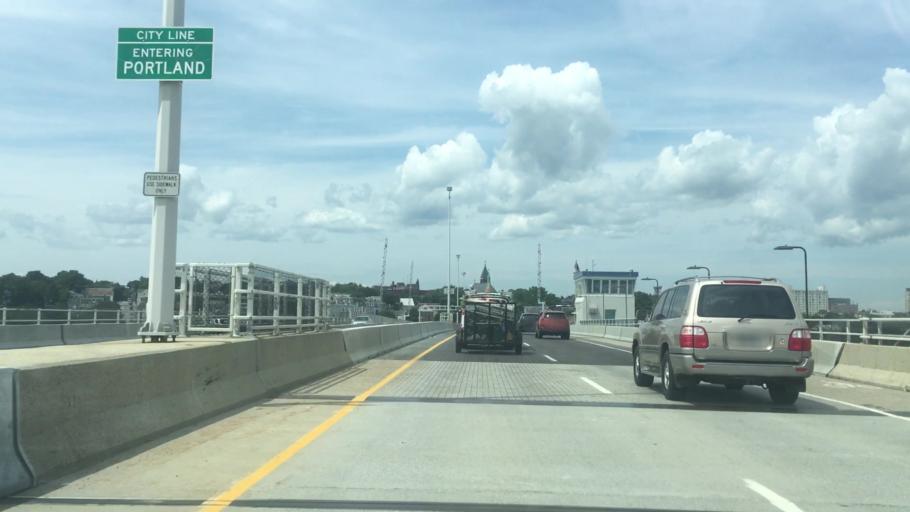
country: US
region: Maine
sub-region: Cumberland County
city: Portland
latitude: 43.6447
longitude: -70.2576
